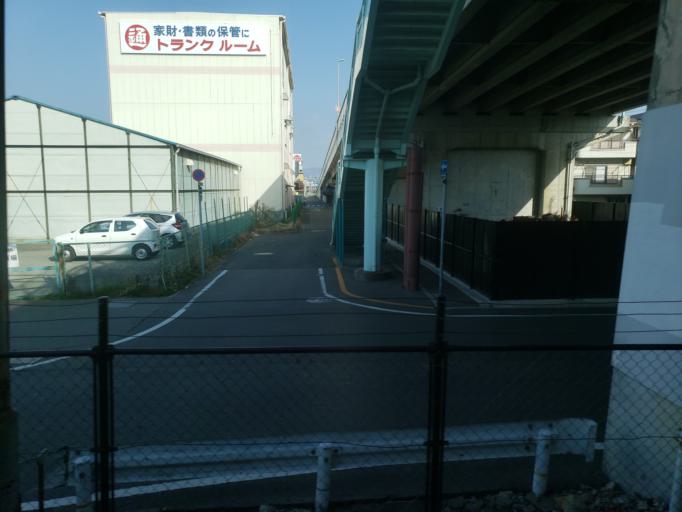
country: JP
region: Hyogo
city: Nishinomiya-hama
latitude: 34.7392
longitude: 135.3656
